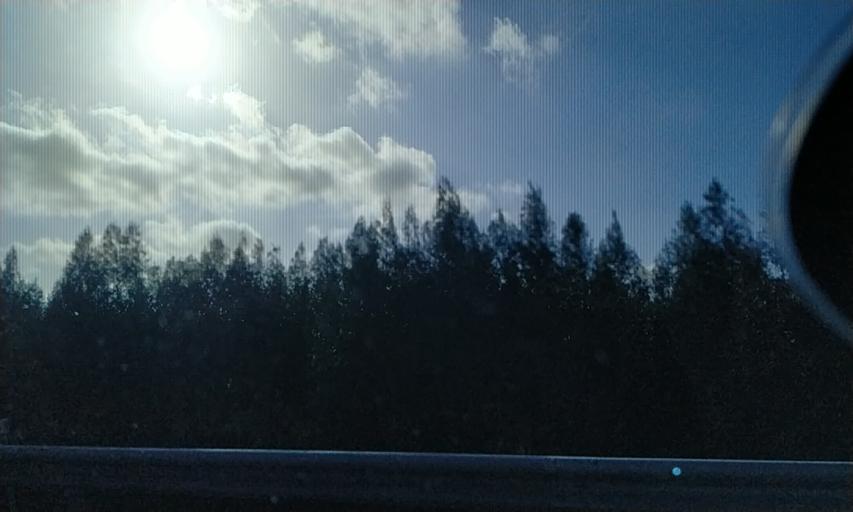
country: PT
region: Lisbon
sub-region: Torres Vedras
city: A dos Cunhados
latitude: 39.1633
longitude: -9.2175
